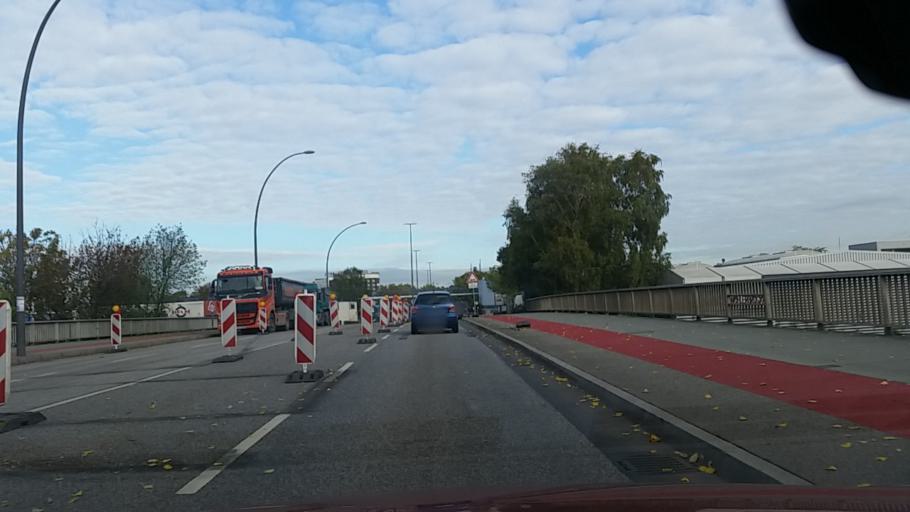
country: DE
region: Hamburg
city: Marienthal
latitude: 53.5334
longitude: 10.0817
